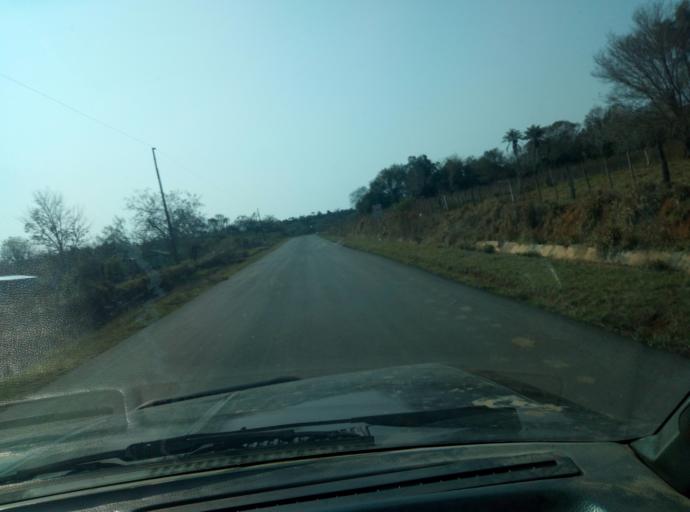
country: PY
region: Caaguazu
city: Carayao
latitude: -25.2632
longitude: -56.2825
